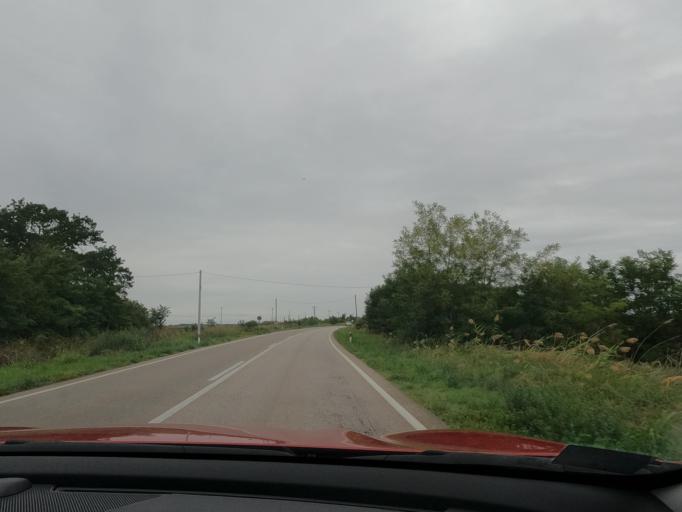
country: RS
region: Autonomna Pokrajina Vojvodina
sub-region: Severnobanatski Okrug
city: Kikinda
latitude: 45.7671
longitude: 20.4233
